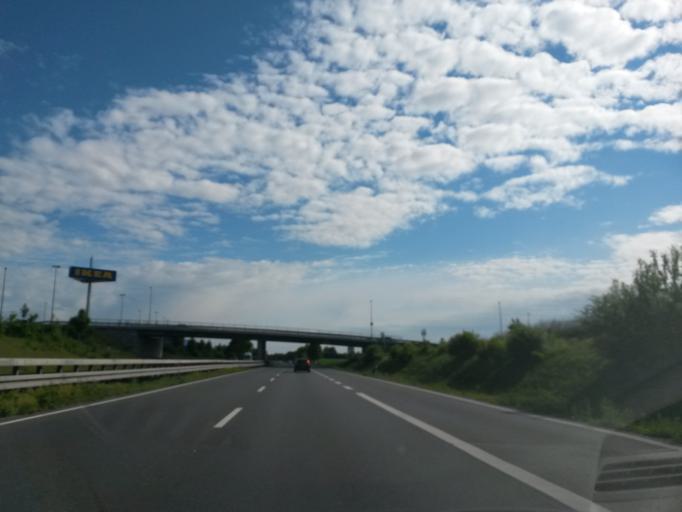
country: DE
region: Bavaria
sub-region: Regierungsbezirk Unterfranken
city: Estenfeld
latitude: 49.8182
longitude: 9.9821
